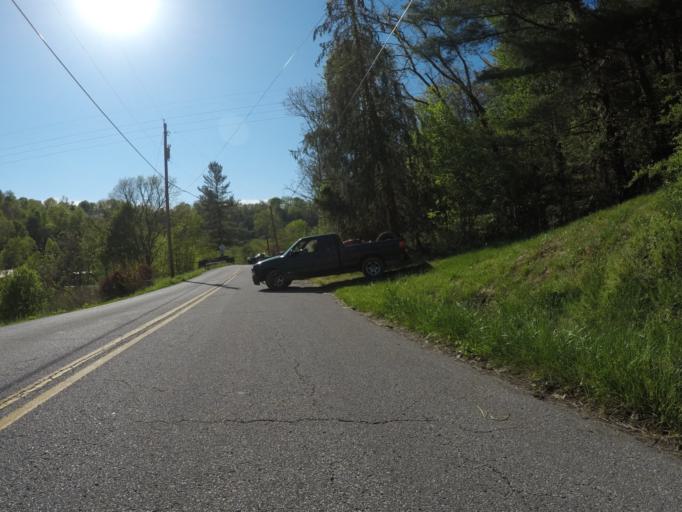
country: US
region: Kentucky
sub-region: Boyd County
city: Catlettsburg
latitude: 38.3992
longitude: -82.6078
